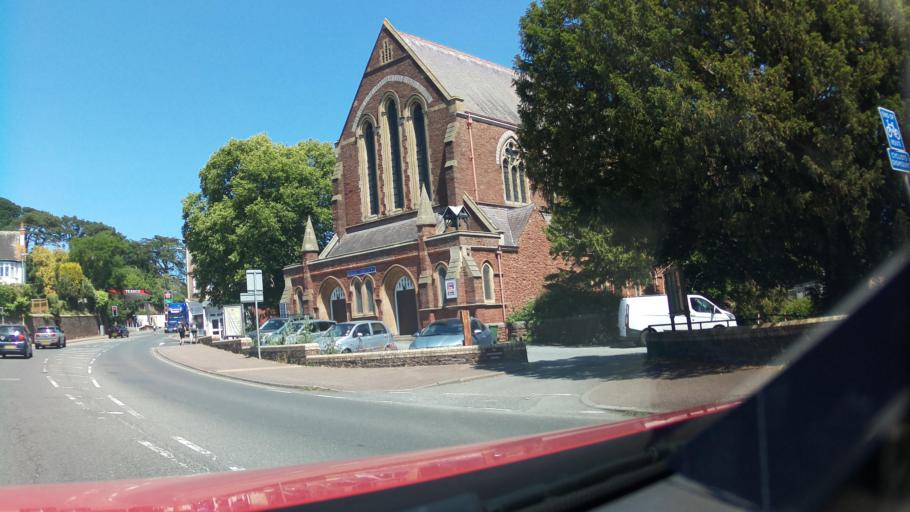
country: GB
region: England
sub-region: Borough of Torbay
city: Paignton
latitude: 50.4401
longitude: -3.5675
